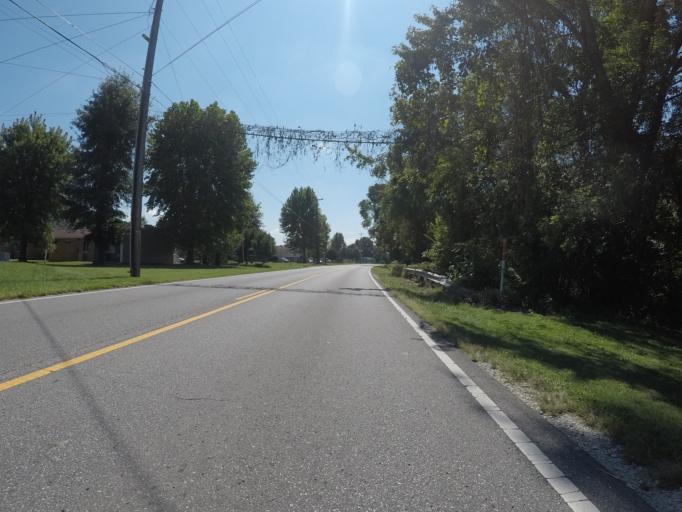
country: US
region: Ohio
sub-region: Lawrence County
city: South Point
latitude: 38.4596
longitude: -82.5979
